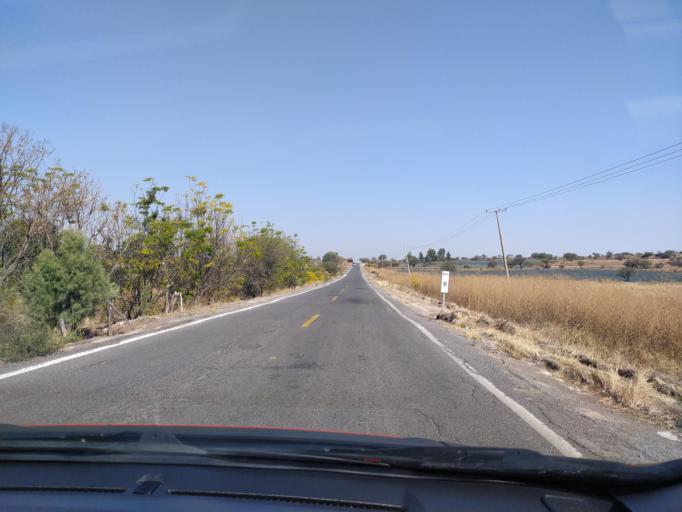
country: MX
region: Guanajuato
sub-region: San Francisco del Rincon
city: San Ignacio de Hidalgo
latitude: 20.8167
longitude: -101.8402
